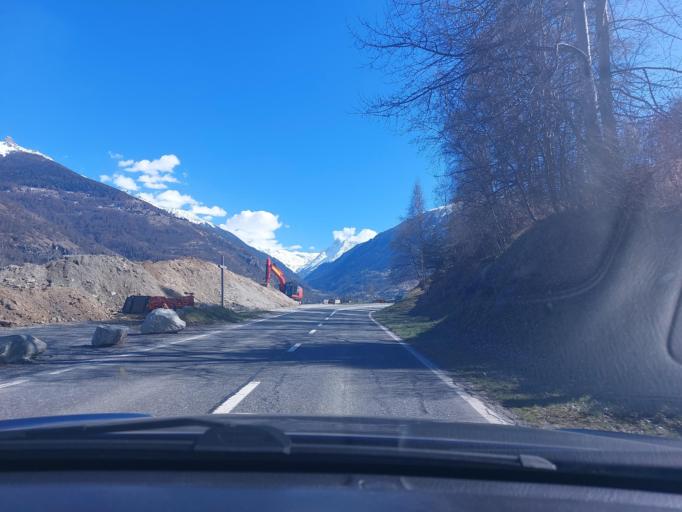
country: CH
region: Valais
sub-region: Herens District
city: Vex
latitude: 46.2012
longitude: 7.4055
